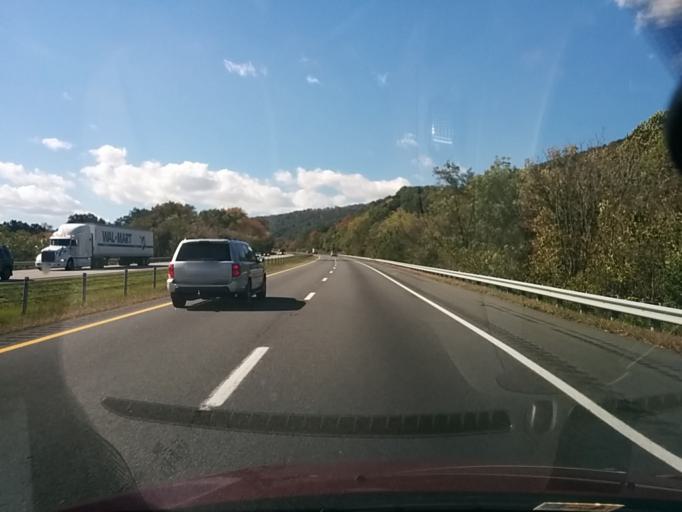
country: US
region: Virginia
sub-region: Albemarle County
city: Crozet
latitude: 38.0475
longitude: -78.7753
